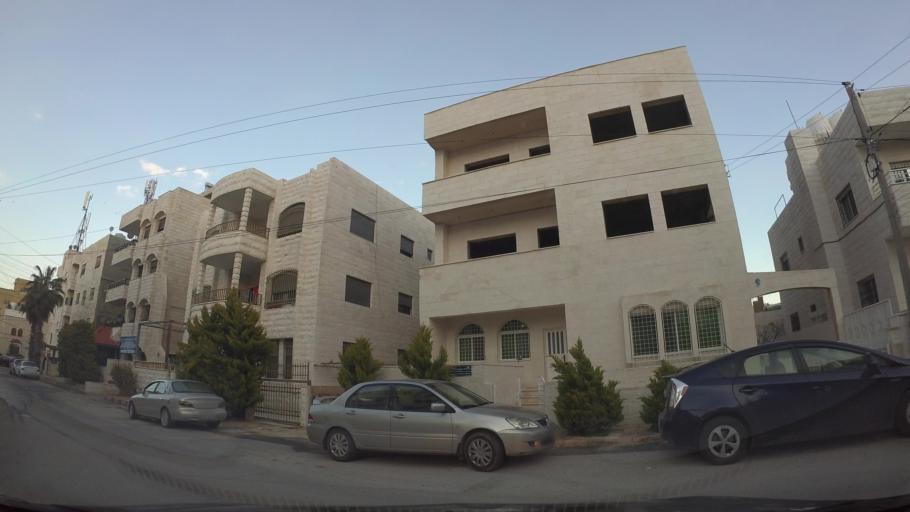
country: JO
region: Amman
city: Al Bunayyat ash Shamaliyah
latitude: 31.9167
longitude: 35.8949
